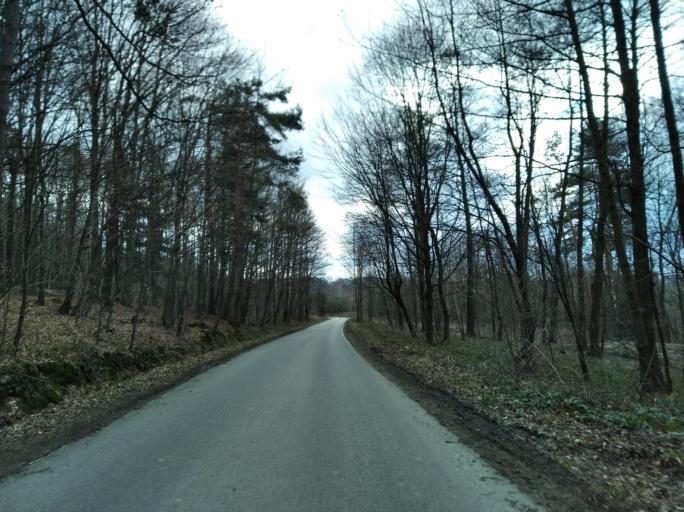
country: PL
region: Subcarpathian Voivodeship
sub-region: Powiat strzyzowski
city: Wysoka Strzyzowska
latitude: 49.7971
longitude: 21.7282
